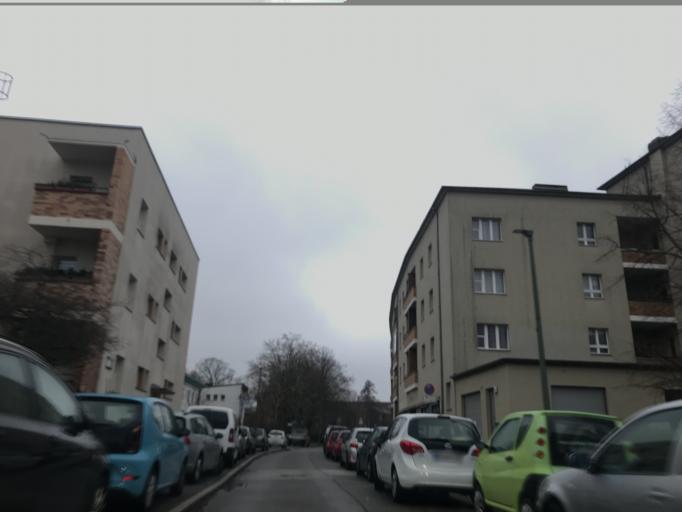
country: DE
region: Berlin
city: Haselhorst
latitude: 52.5459
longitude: 13.2339
